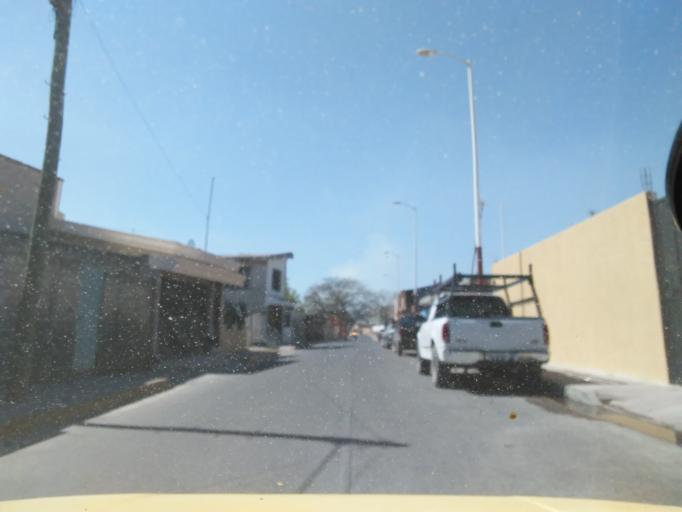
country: MX
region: Nayarit
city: Xalisco
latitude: 21.4407
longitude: -104.8981
